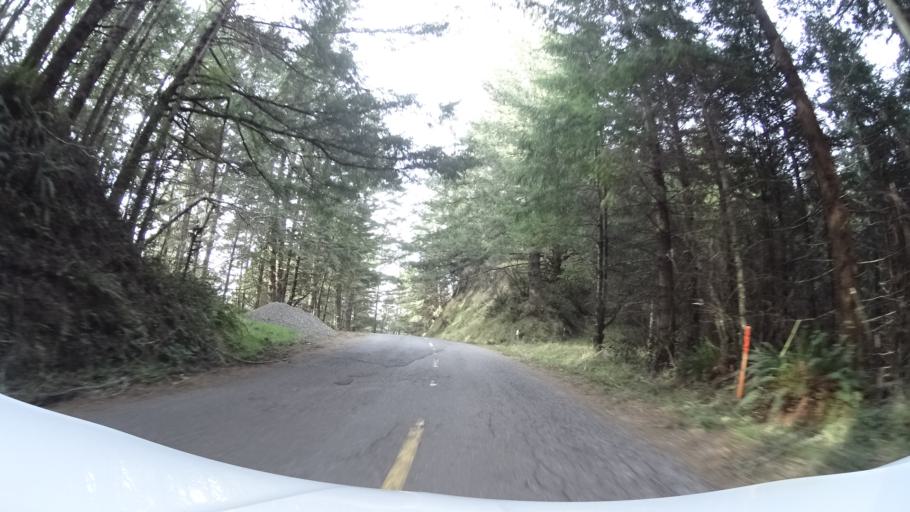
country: US
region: California
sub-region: Humboldt County
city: Ferndale
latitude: 40.5255
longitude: -124.2668
